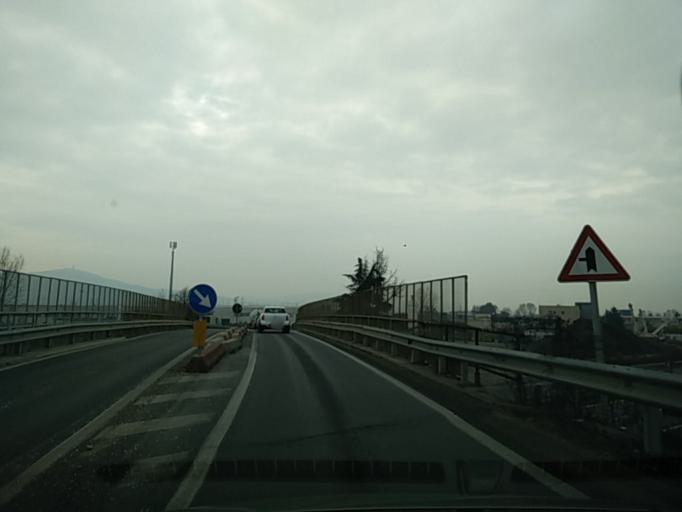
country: IT
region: Piedmont
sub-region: Provincia di Torino
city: Settimo Torinese
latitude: 45.1362
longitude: 7.7364
